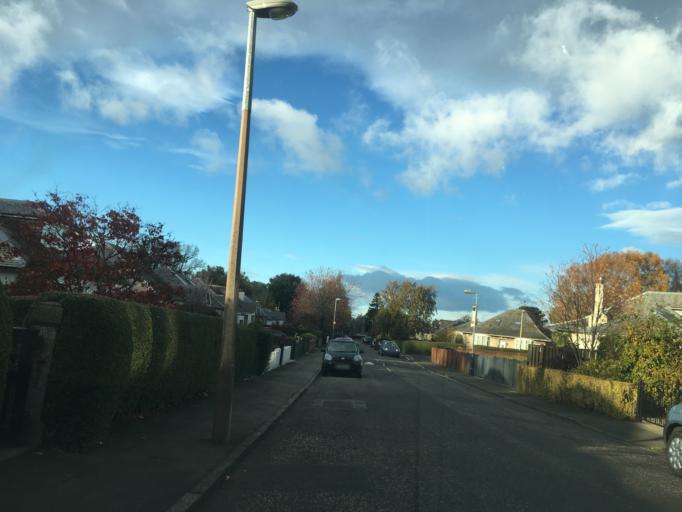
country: GB
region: Scotland
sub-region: Edinburgh
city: Colinton
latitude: 55.9175
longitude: -3.2471
